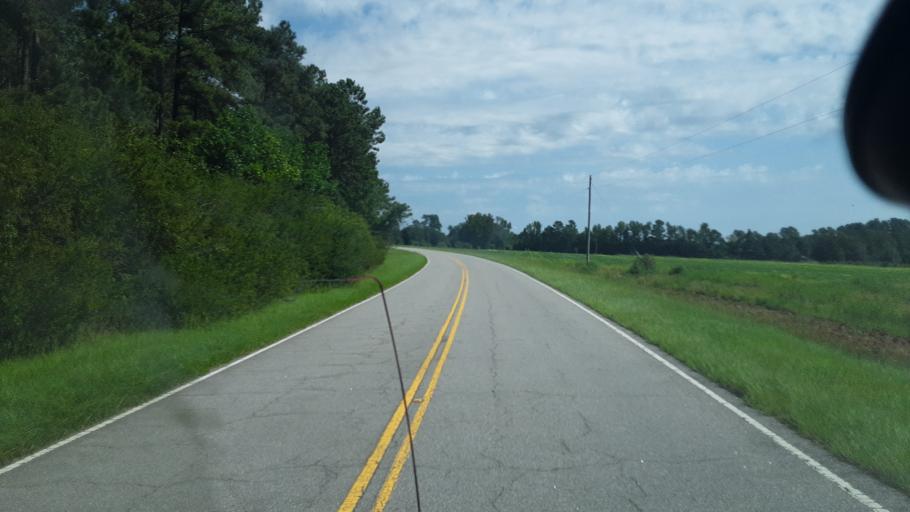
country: US
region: South Carolina
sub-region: Hampton County
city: Hampton
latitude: 33.0381
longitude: -81.0342
